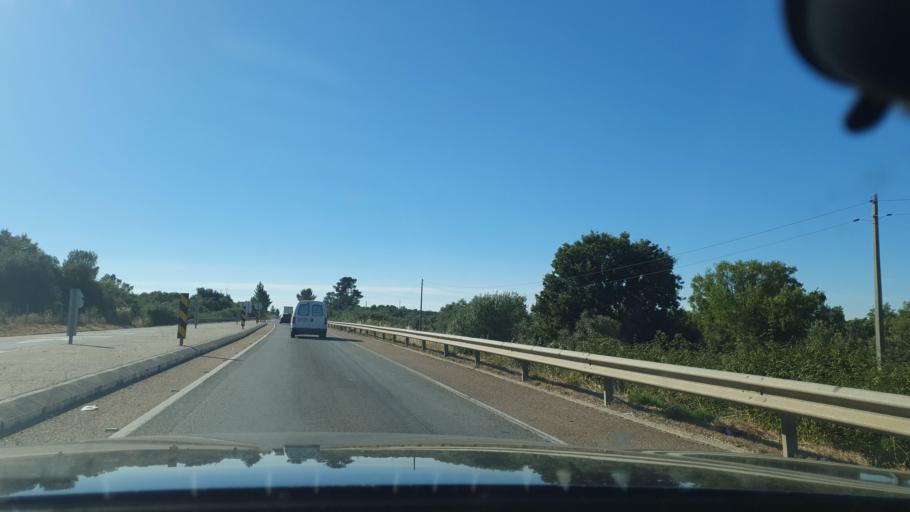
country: PT
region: Evora
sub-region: Borba
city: Borba
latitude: 38.7912
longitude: -7.4594
